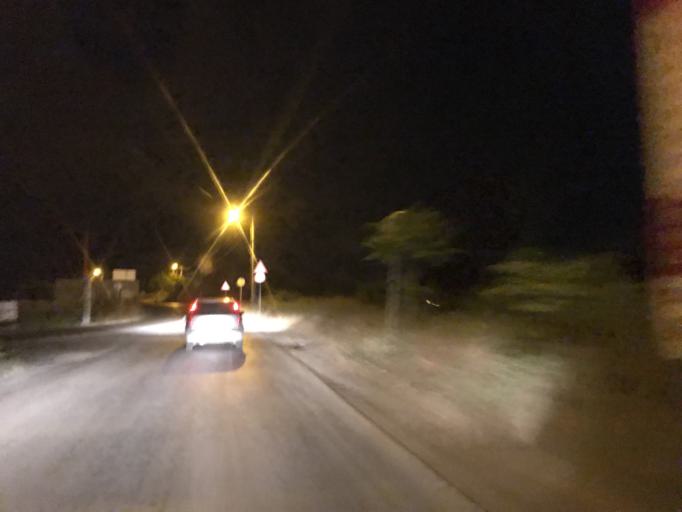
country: RS
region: Central Serbia
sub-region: Belgrade
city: Zvezdara
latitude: 44.7799
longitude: 20.5475
